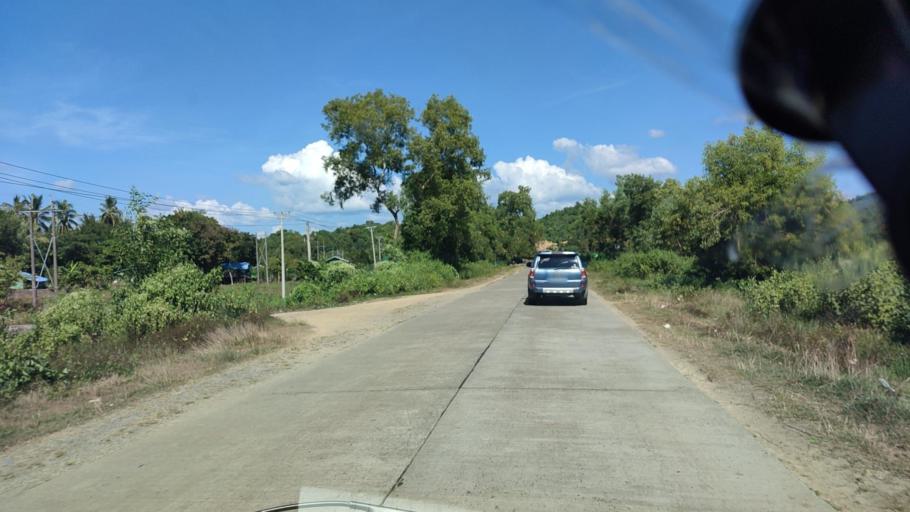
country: MM
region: Rakhine
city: Sittwe
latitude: 20.3934
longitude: 93.3286
